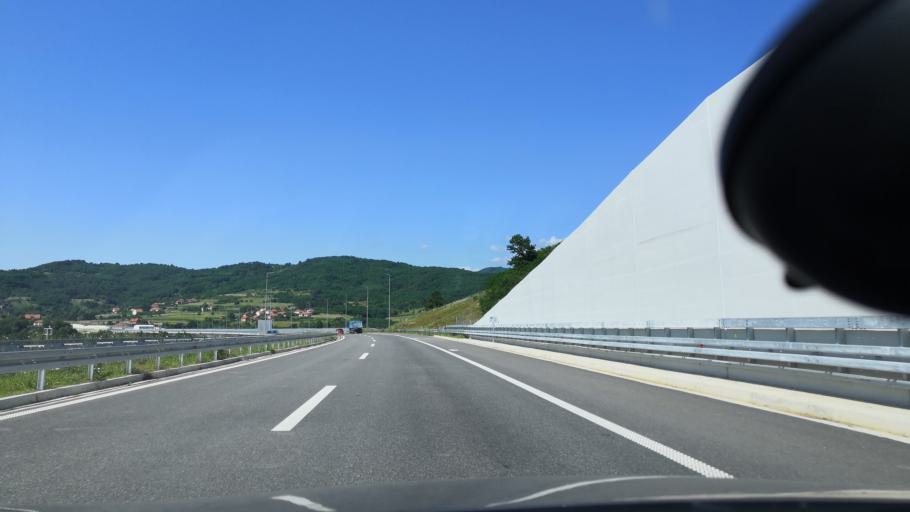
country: RS
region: Central Serbia
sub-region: Pcinjski Okrug
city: Vladicin Han
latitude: 42.7175
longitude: 22.0755
